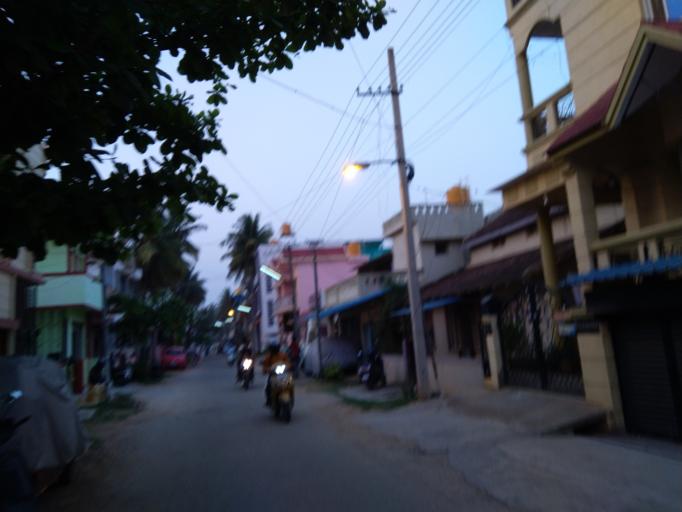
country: IN
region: Karnataka
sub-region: Hassan
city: Hassan
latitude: 13.0109
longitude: 76.1090
